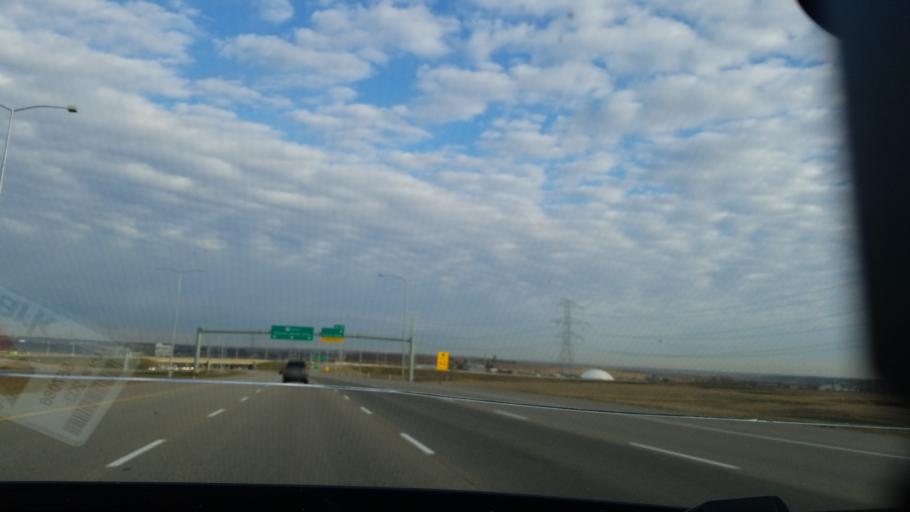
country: CA
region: Alberta
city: Sherwood Park
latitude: 53.5805
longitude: -113.3442
